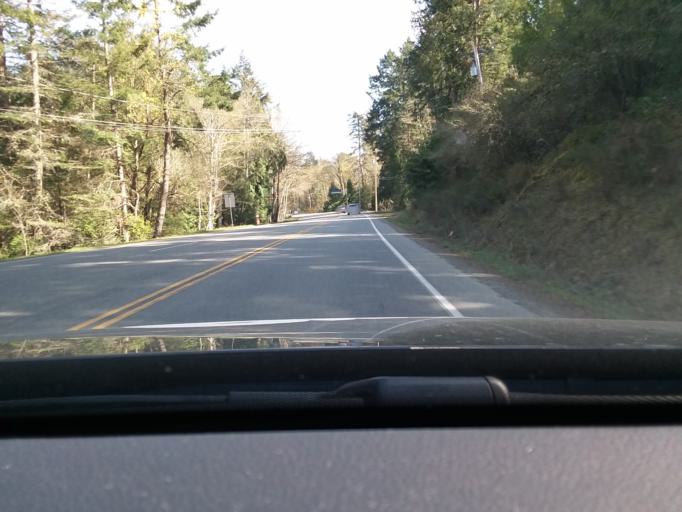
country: CA
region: British Columbia
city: North Saanich
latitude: 48.8513
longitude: -123.4539
